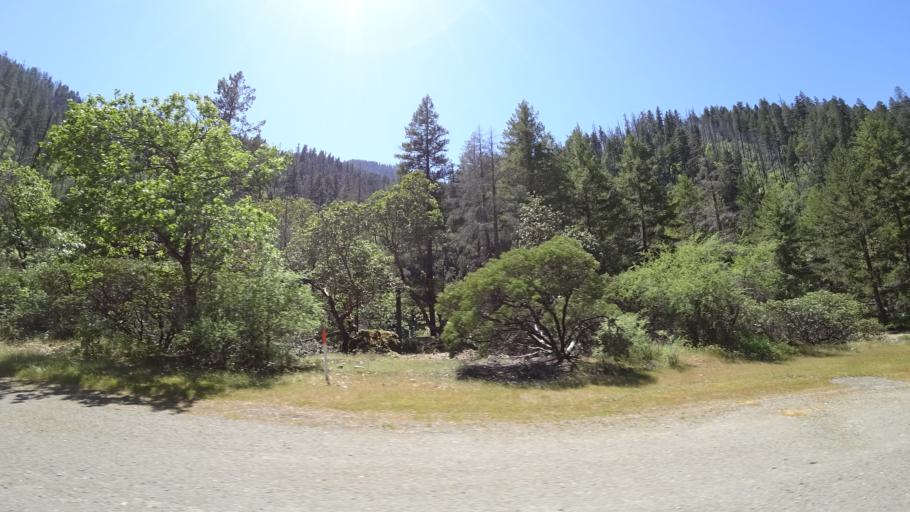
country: US
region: California
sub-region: Trinity County
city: Hayfork
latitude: 40.7669
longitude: -123.3062
